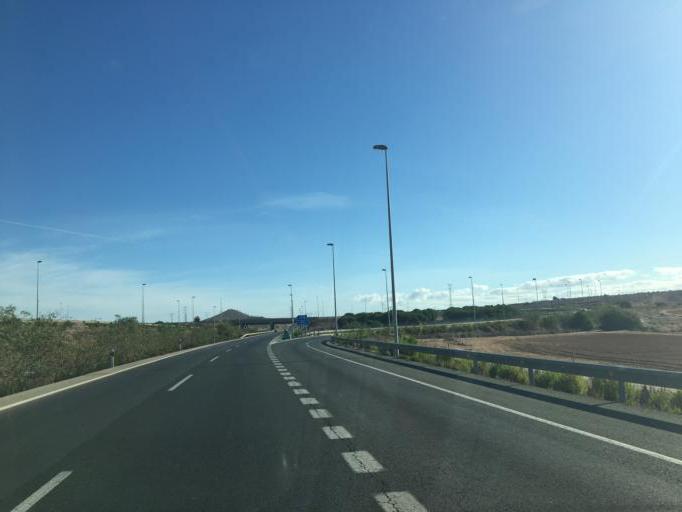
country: ES
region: Murcia
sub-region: Murcia
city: Cartagena
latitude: 37.6238
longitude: -0.9455
